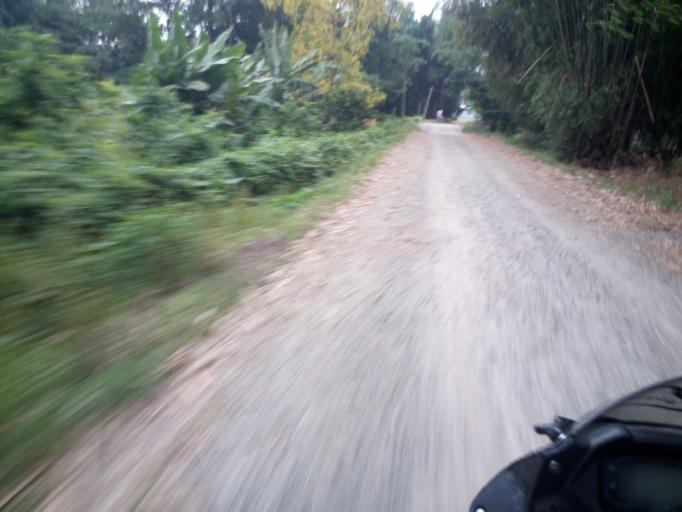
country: IN
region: Assam
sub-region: Darrang
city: Kharupatia
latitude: 26.6513
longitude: 92.2444
